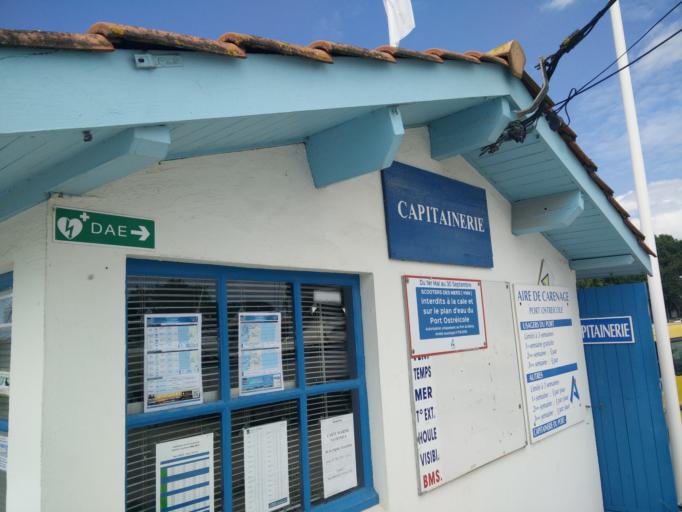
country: FR
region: Aquitaine
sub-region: Departement de la Gironde
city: Andernos-les-Bains
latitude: 44.7434
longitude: -1.1076
